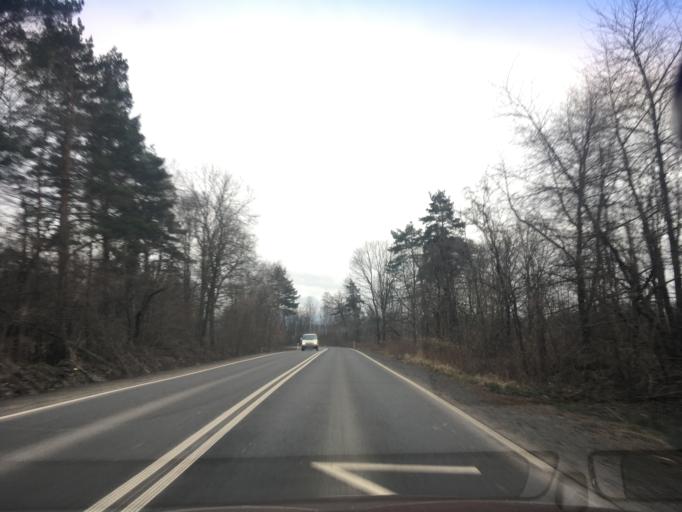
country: DE
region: Saxony
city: Hirschfelde
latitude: 50.9387
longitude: 14.9200
